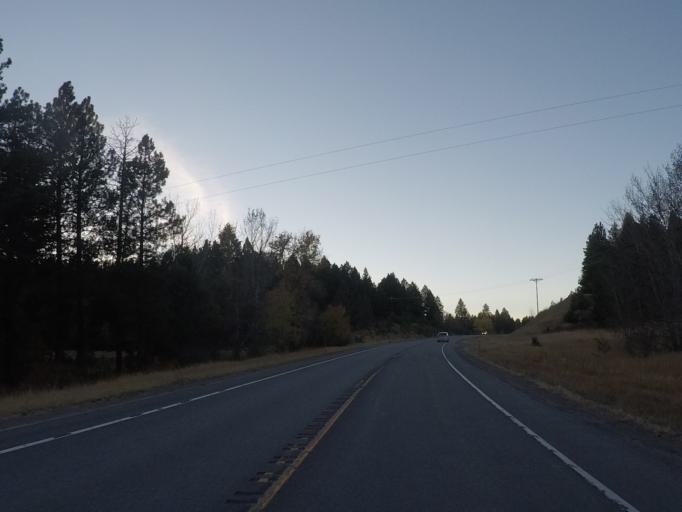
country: US
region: Montana
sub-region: Lewis and Clark County
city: Lincoln
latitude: 47.0083
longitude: -113.0558
